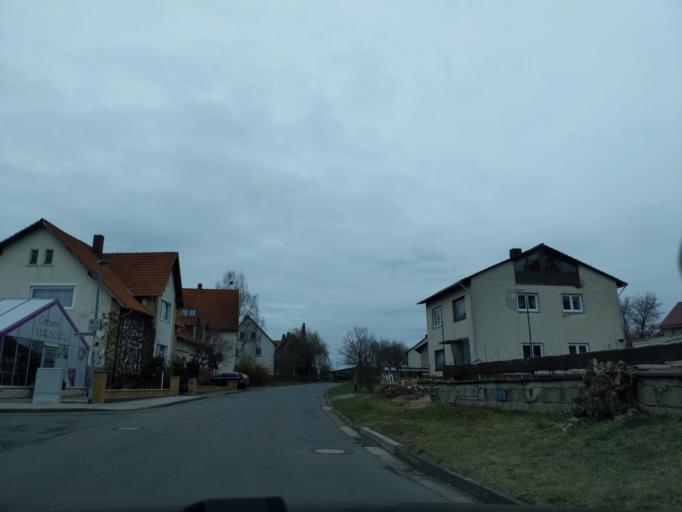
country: DE
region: Hesse
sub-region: Regierungsbezirk Kassel
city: Volkmarsen
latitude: 51.3479
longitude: 9.0868
